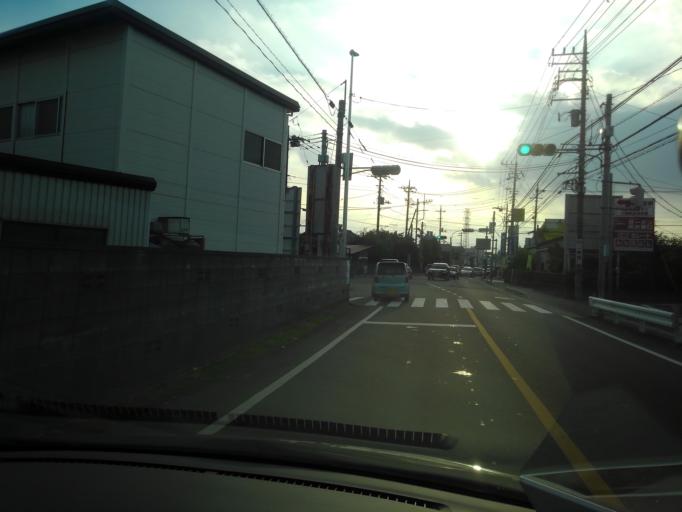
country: JP
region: Saitama
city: Tokorozawa
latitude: 35.7913
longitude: 139.4994
